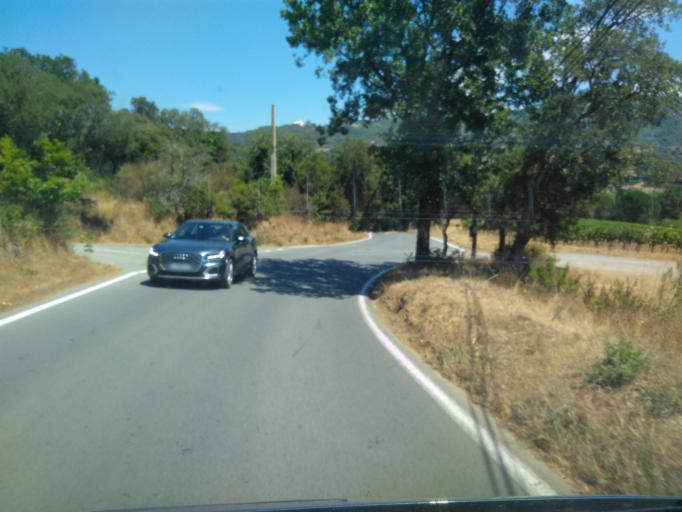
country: FR
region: Provence-Alpes-Cote d'Azur
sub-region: Departement du Var
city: La Croix-Valmer
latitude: 43.2125
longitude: 6.5772
